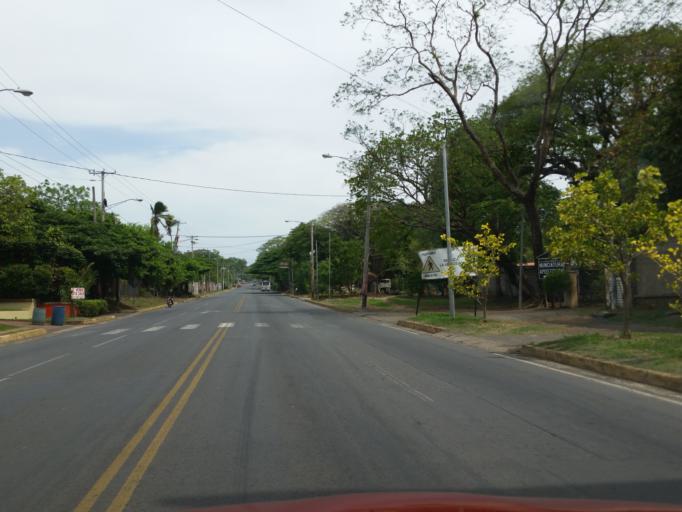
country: NI
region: Managua
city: Ciudad Sandino
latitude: 12.0910
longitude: -86.3239
